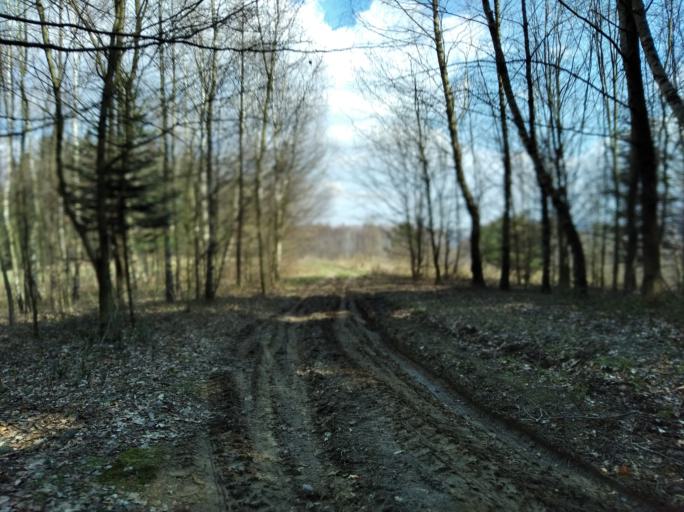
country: PL
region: Subcarpathian Voivodeship
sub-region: Powiat strzyzowski
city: Strzyzow
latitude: 49.8259
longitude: 21.8021
